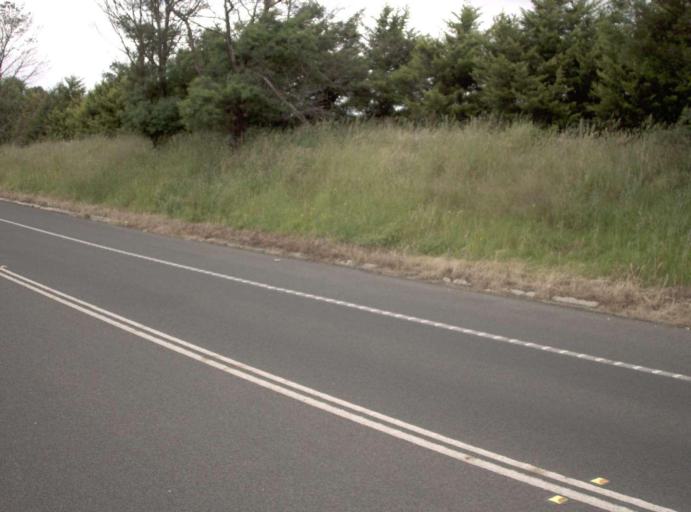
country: AU
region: Victoria
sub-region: Baw Baw
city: Warragul
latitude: -38.4479
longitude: 145.8915
